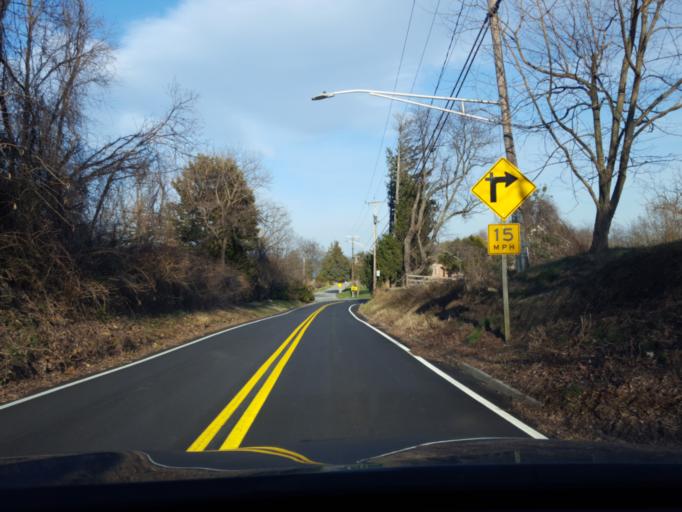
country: US
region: Maryland
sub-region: Anne Arundel County
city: Deale
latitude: 38.7546
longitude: -76.5617
